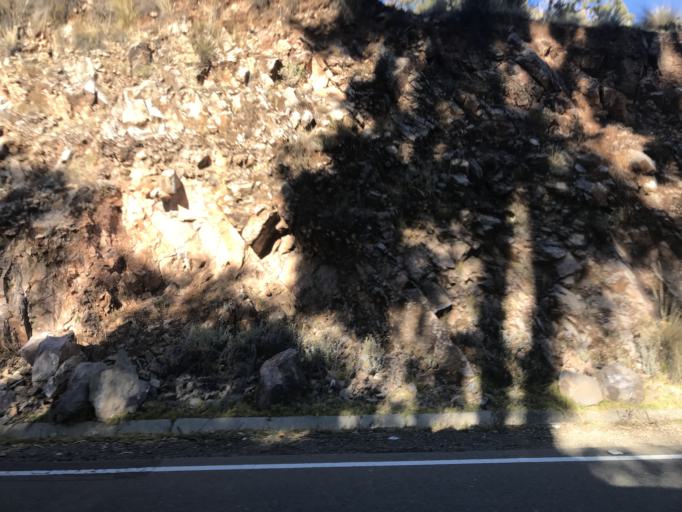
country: BO
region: La Paz
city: San Pedro
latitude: -16.2271
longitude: -68.8523
